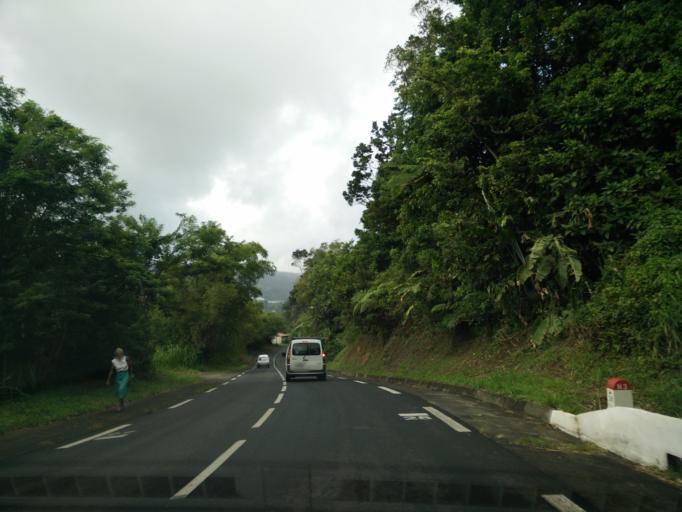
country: MQ
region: Martinique
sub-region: Martinique
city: Le Morne-Rouge
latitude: 14.7708
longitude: -61.1297
